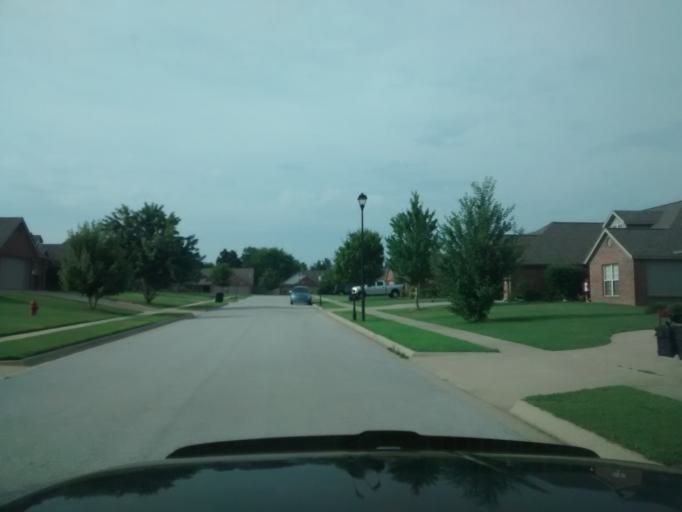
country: US
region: Arkansas
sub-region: Washington County
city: Farmington
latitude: 36.0740
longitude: -94.2839
